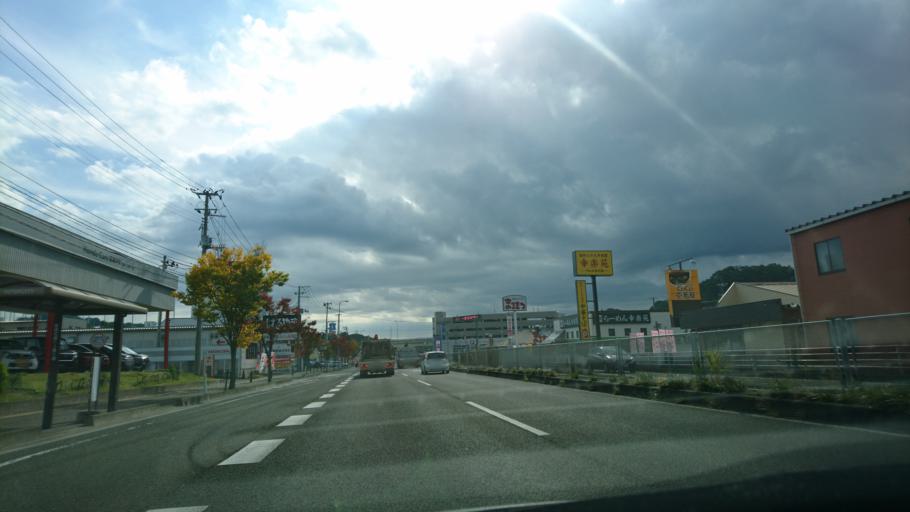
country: JP
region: Miyagi
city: Tomiya
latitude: 38.3508
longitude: 140.8740
